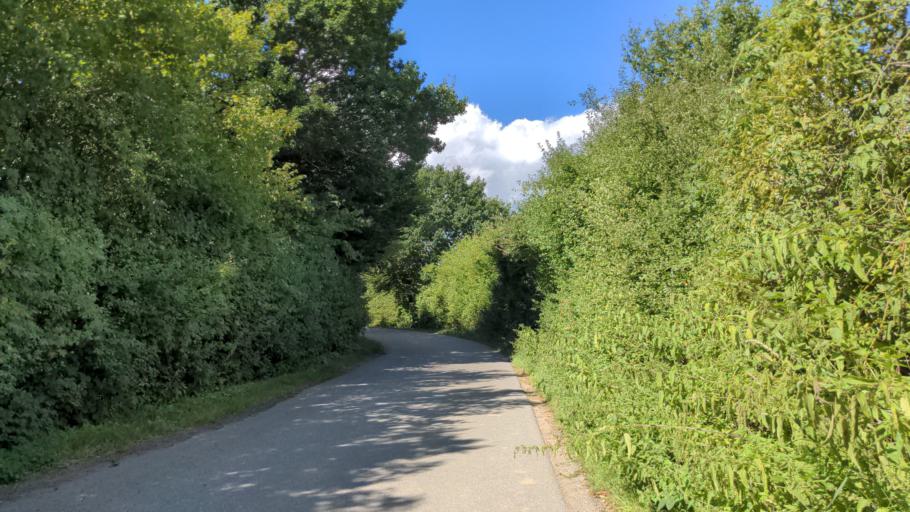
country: DE
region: Schleswig-Holstein
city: Beschendorf
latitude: 54.1811
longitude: 10.8275
